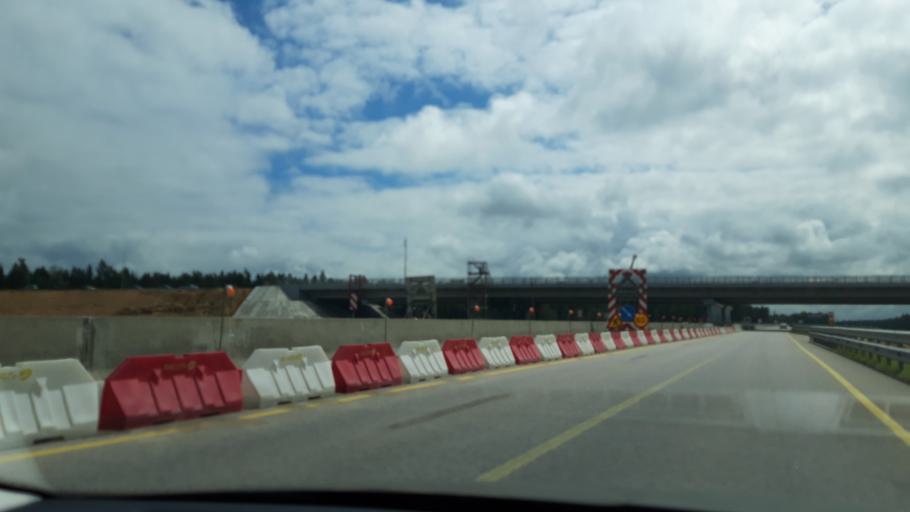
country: RU
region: Moskovskaya
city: Mendeleyevo
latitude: 56.0871
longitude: 37.2037
